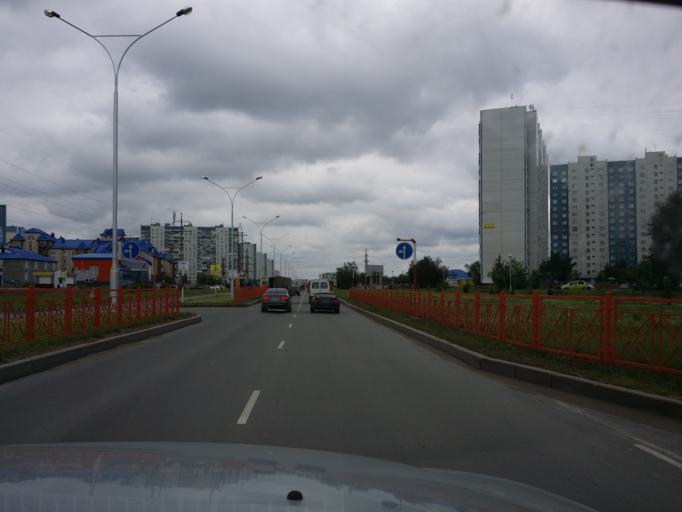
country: RU
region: Khanty-Mansiyskiy Avtonomnyy Okrug
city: Nizhnevartovsk
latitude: 60.9568
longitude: 76.5702
